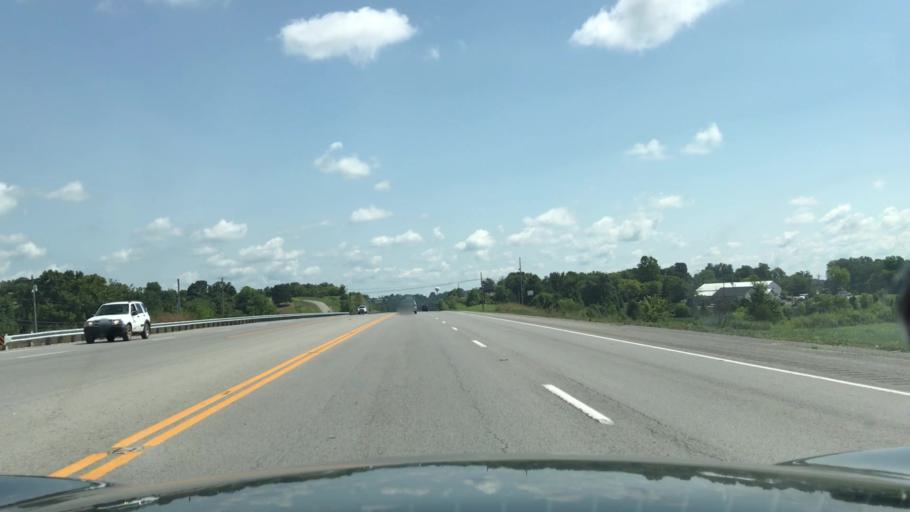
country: US
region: Kentucky
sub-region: Adair County
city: Columbia
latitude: 37.0798
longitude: -85.3340
